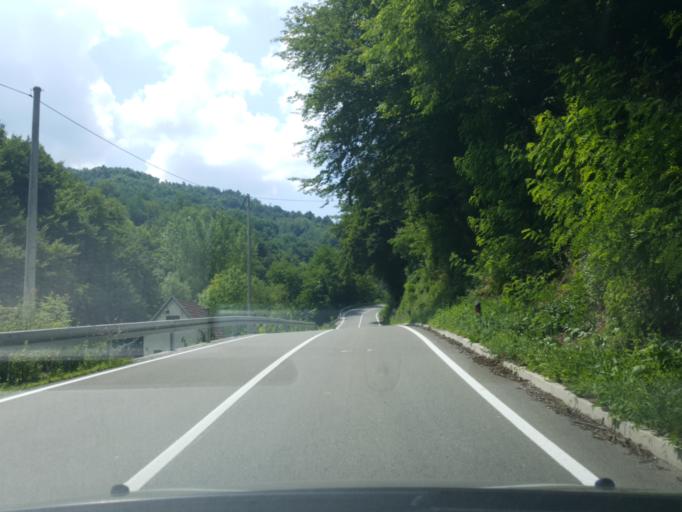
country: RS
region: Central Serbia
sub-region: Sumadijski Okrug
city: Arangelovac
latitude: 44.1654
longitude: 20.5142
